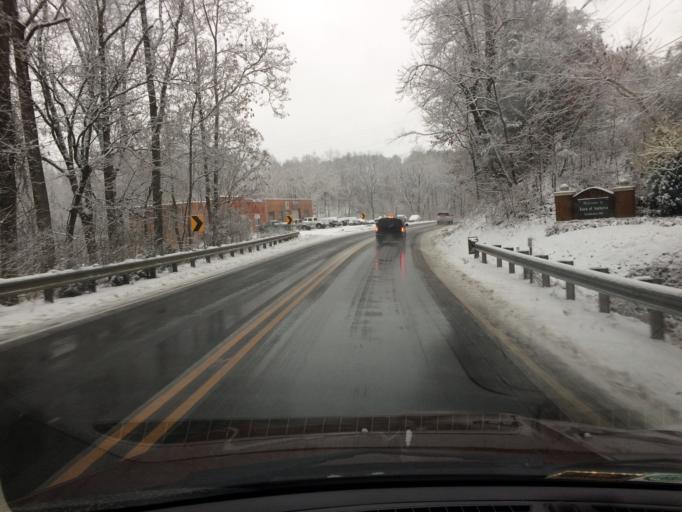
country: US
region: Virginia
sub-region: Amherst County
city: Amherst
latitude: 37.5957
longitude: -79.0543
